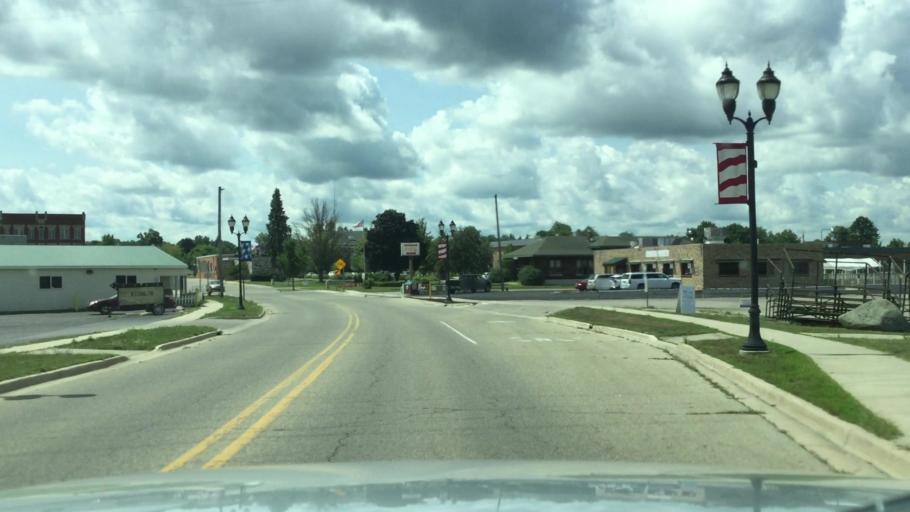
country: US
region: Michigan
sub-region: Ionia County
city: Belding
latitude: 43.0998
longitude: -85.2285
